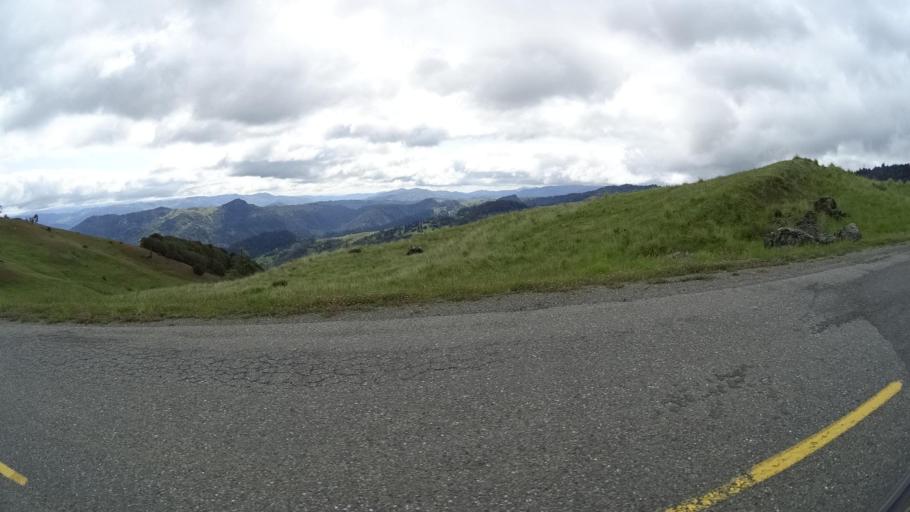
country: US
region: California
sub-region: Humboldt County
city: Redway
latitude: 40.1081
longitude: -123.6708
